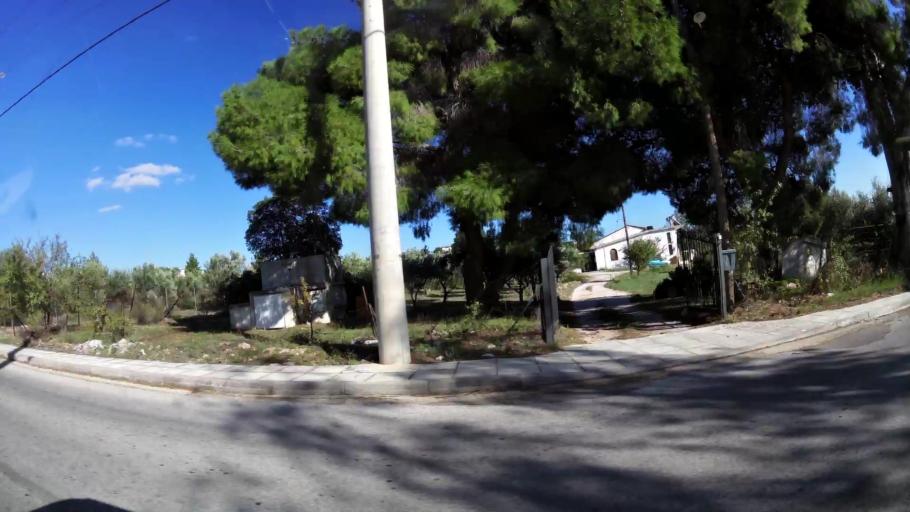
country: GR
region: Attica
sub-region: Nomarchia Anatolikis Attikis
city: Anthousa
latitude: 38.0213
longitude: 23.8674
